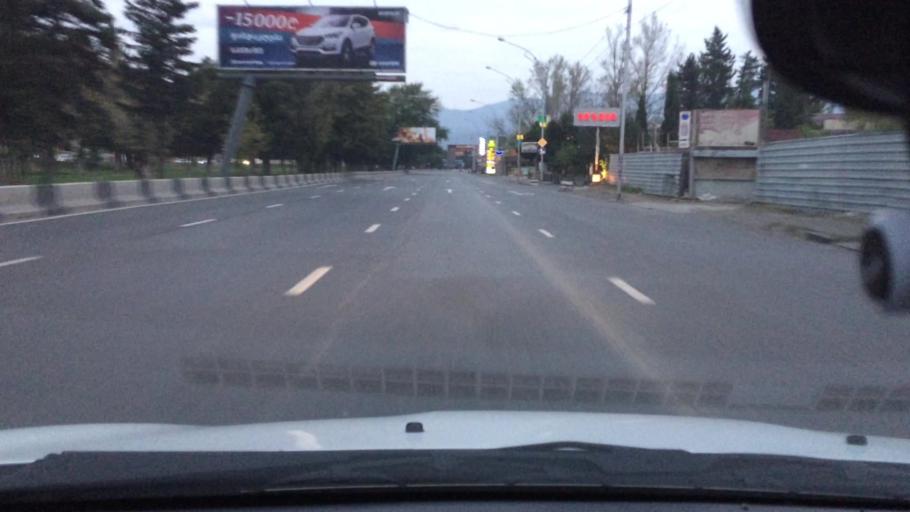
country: GE
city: Zahesi
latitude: 41.7754
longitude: 44.7690
